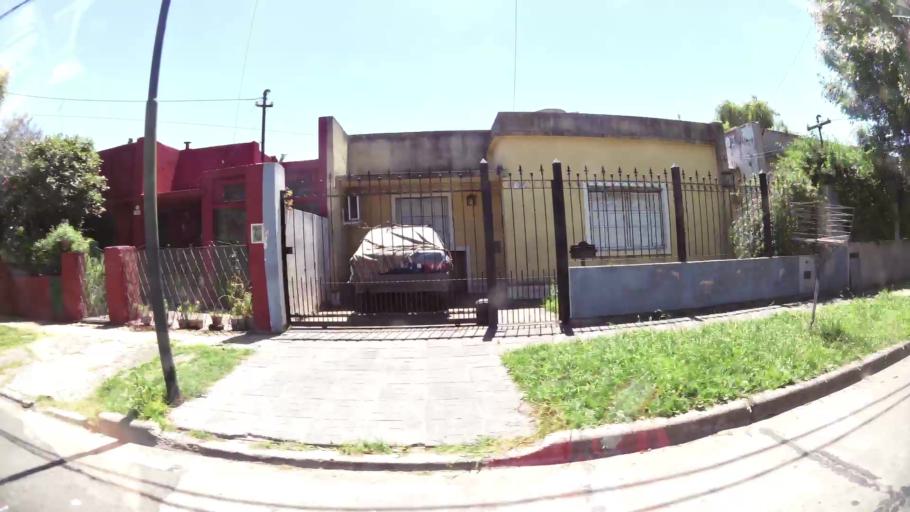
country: AR
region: Buenos Aires
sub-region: Partido de Tigre
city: Tigre
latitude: -34.4952
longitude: -58.5784
